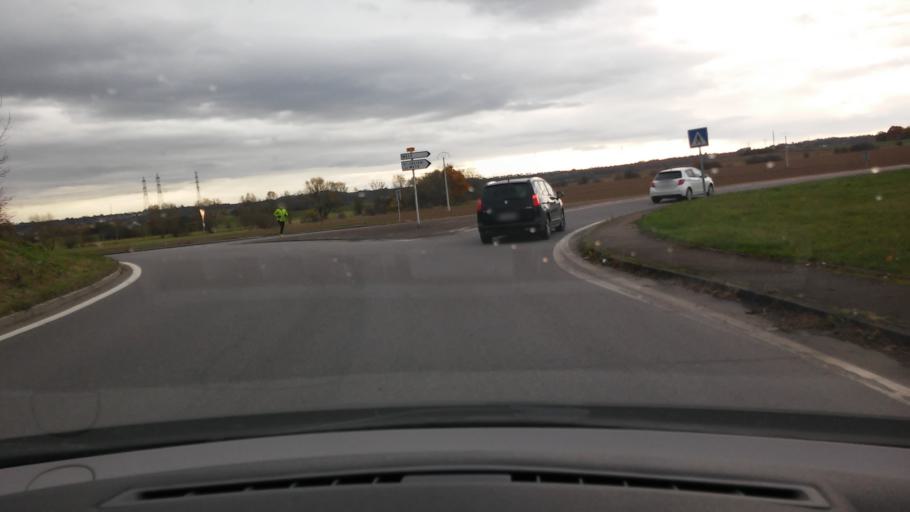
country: FR
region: Lorraine
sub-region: Departement de la Moselle
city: Argancy
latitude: 49.1704
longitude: 6.2142
